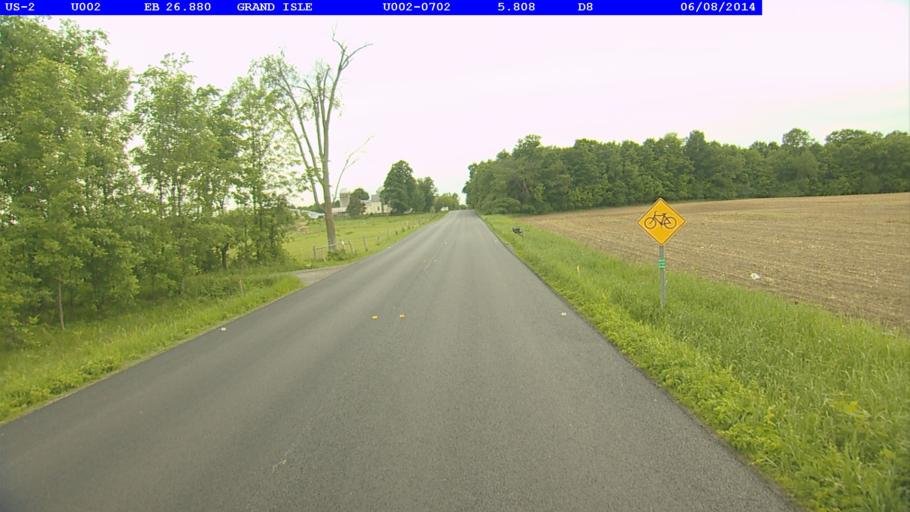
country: US
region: New York
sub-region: Clinton County
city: Cumberland Head
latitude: 44.6862
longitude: -73.3118
